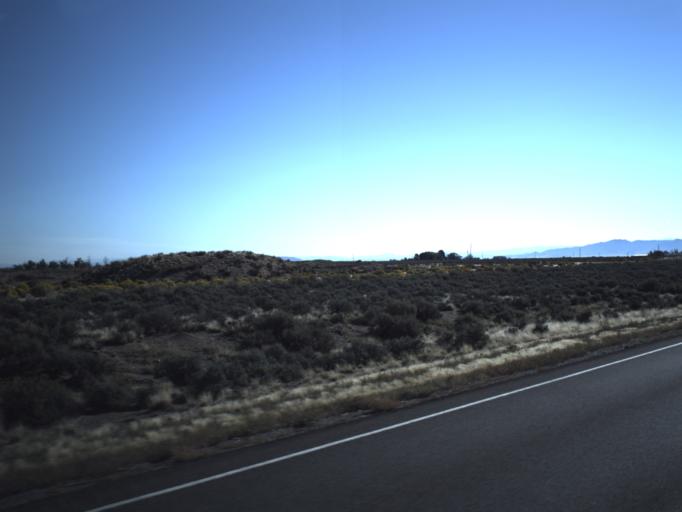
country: US
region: Utah
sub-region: Washington County
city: Enterprise
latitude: 37.7693
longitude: -113.8259
